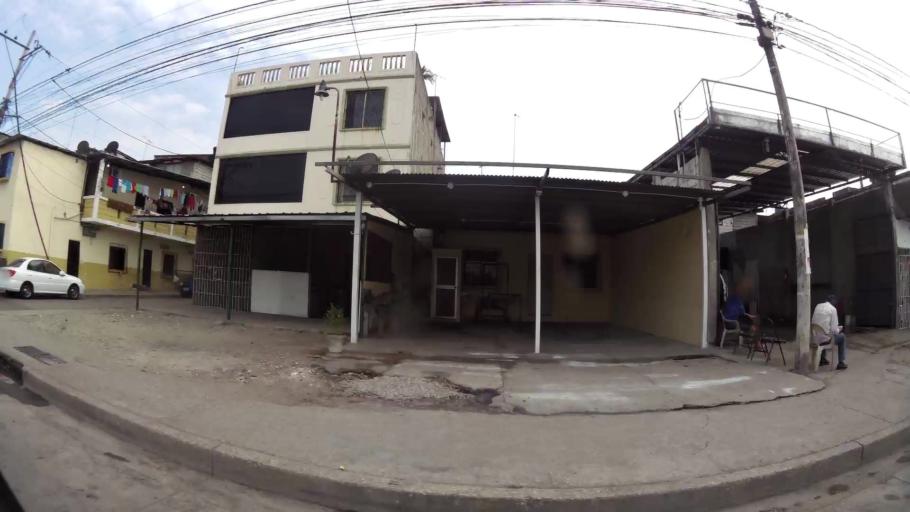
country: EC
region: Guayas
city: Guayaquil
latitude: -2.2511
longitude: -79.8923
